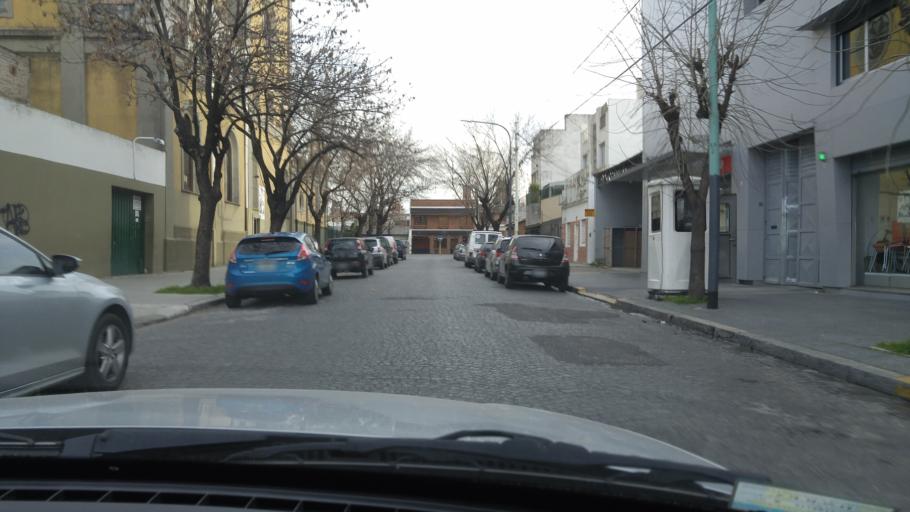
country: AR
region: Buenos Aires F.D.
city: Villa Santa Rita
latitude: -34.6287
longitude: -58.5146
